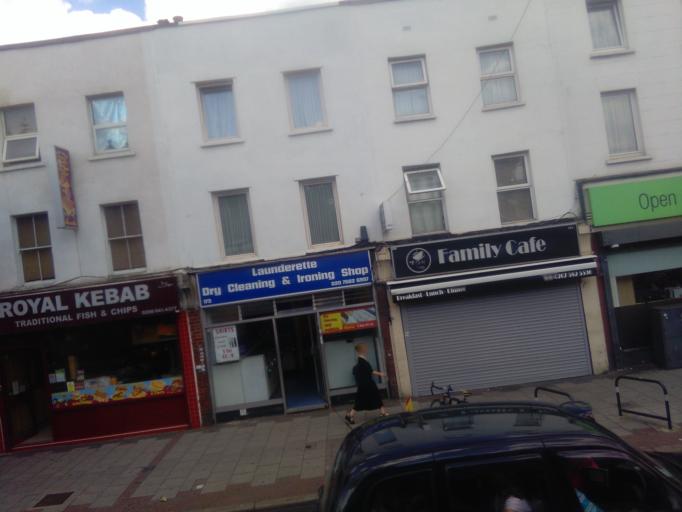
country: GB
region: England
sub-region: Greater London
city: Kennington
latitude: 51.4783
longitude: -0.1031
